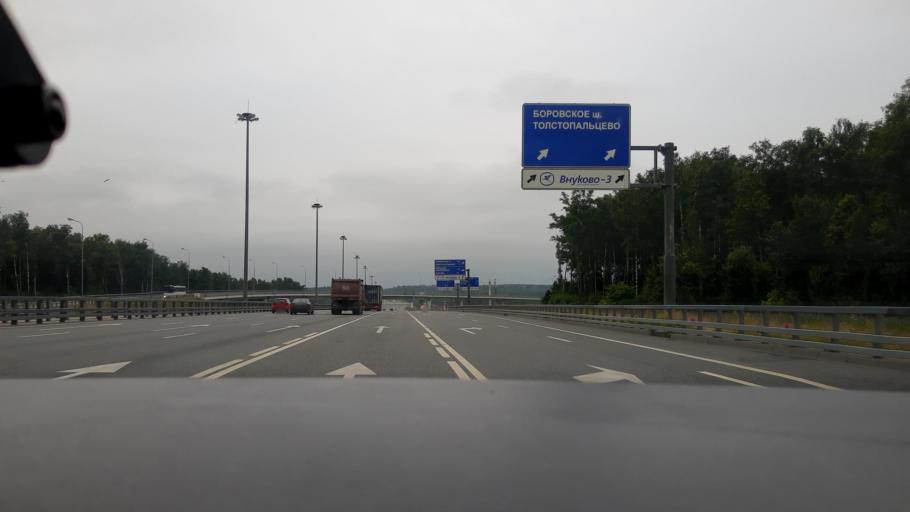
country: RU
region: Moscow
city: Vnukovo
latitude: 55.5749
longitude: 37.2154
